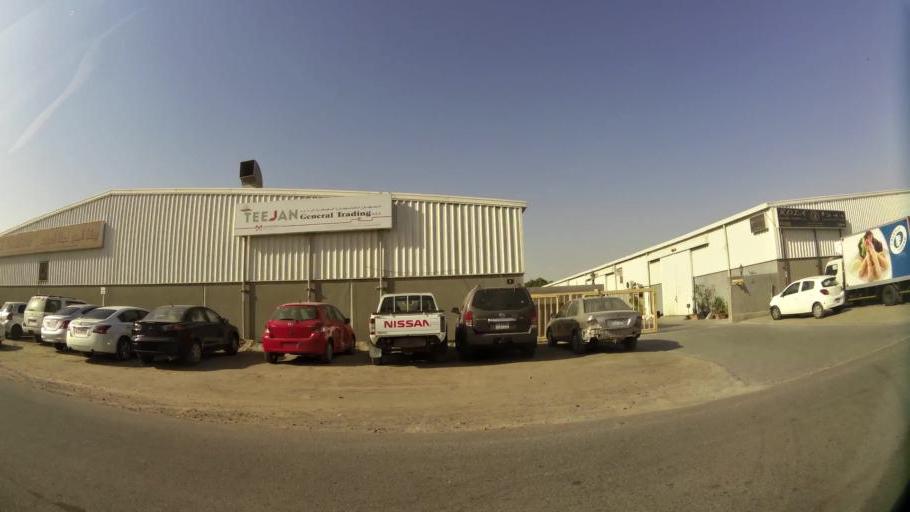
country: AE
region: Ash Shariqah
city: Sharjah
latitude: 25.2841
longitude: 55.3816
